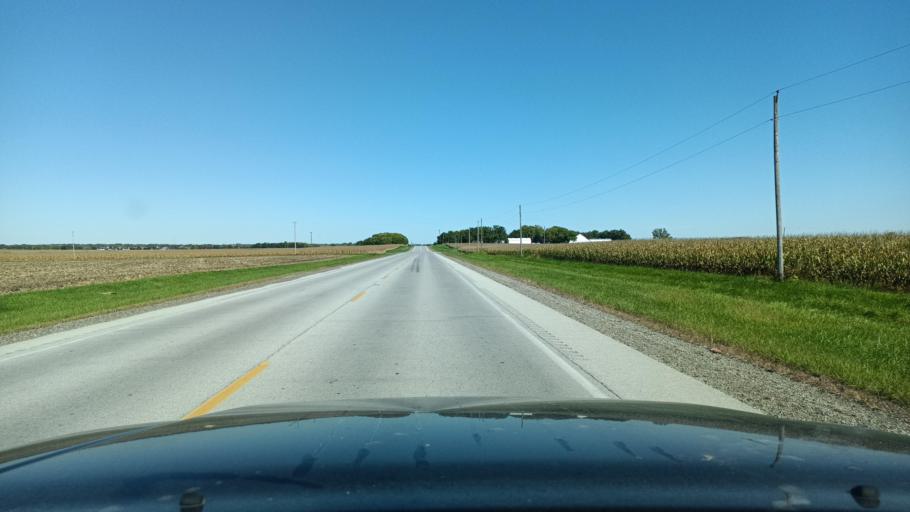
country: US
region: Illinois
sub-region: Champaign County
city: Philo
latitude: 40.0674
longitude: -88.1619
